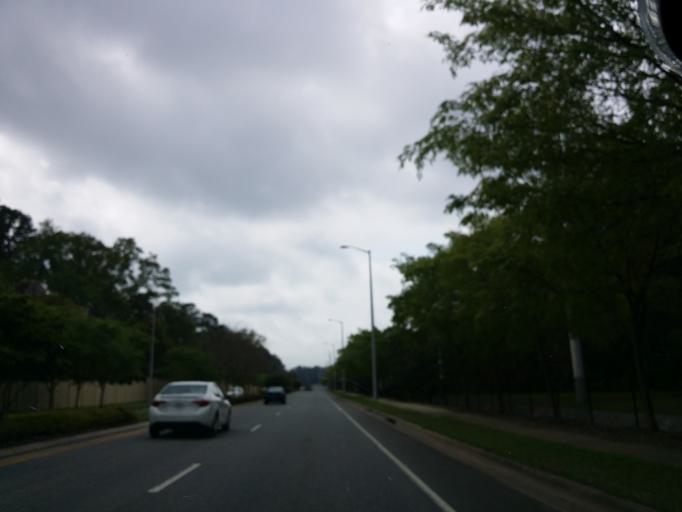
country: US
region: Florida
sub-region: Leon County
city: Tallahassee
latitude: 30.4706
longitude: -84.2439
